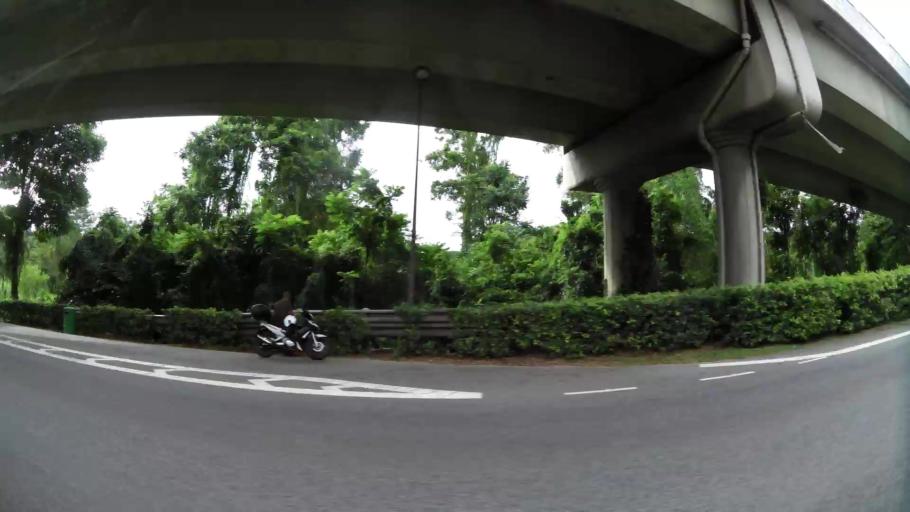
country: MY
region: Johor
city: Johor Bahru
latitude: 1.3666
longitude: 103.7094
